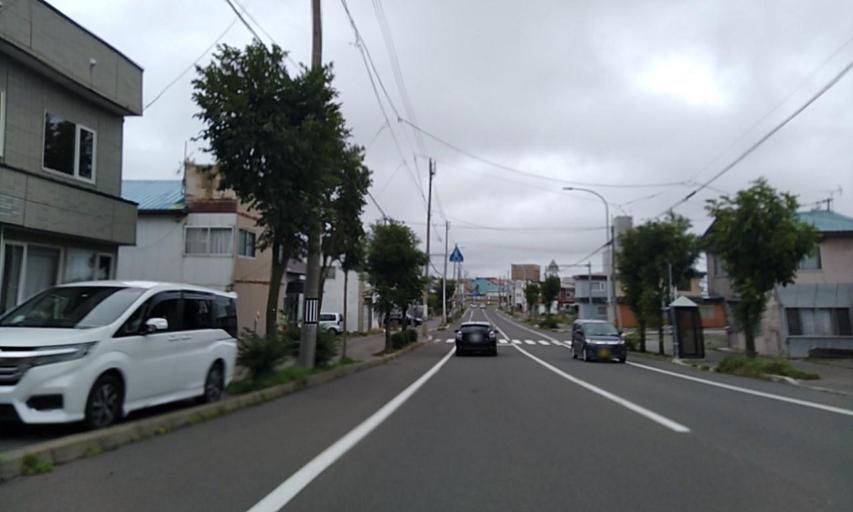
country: JP
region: Hokkaido
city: Nemuro
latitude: 43.3318
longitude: 145.5750
